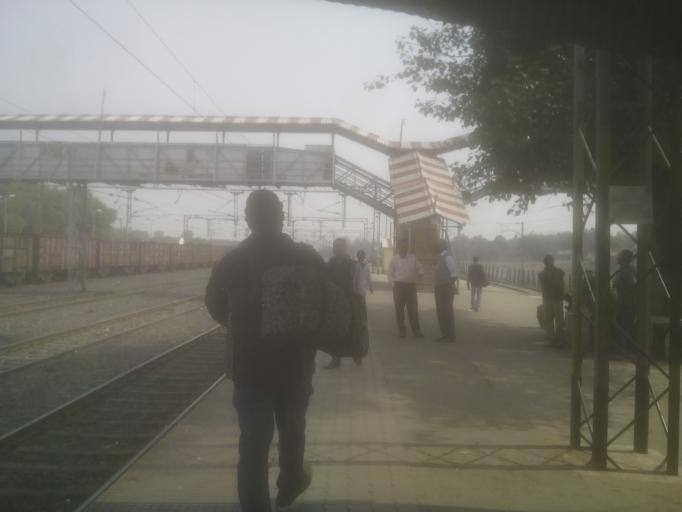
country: IN
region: Jharkhand
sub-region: Bokaro
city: Dugda
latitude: 23.7554
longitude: 86.1203
